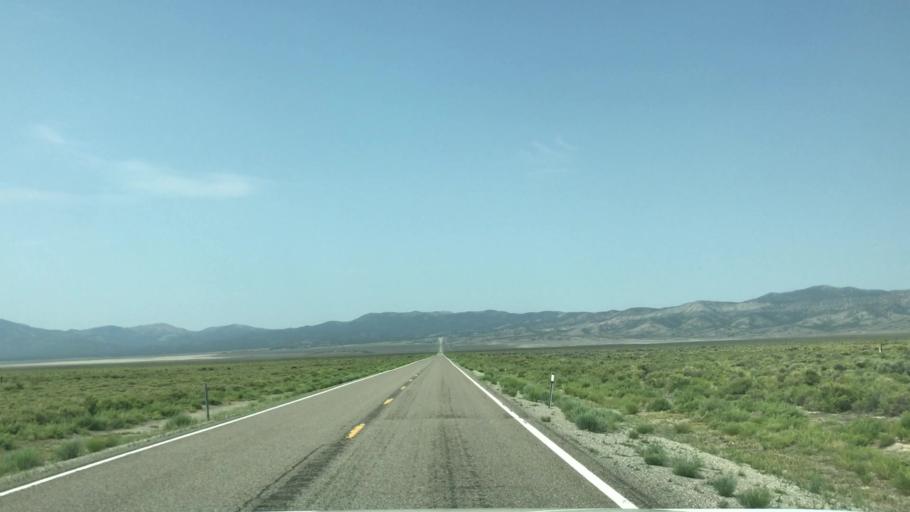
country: US
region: Nevada
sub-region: White Pine County
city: Ely
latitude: 39.0627
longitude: -114.4711
